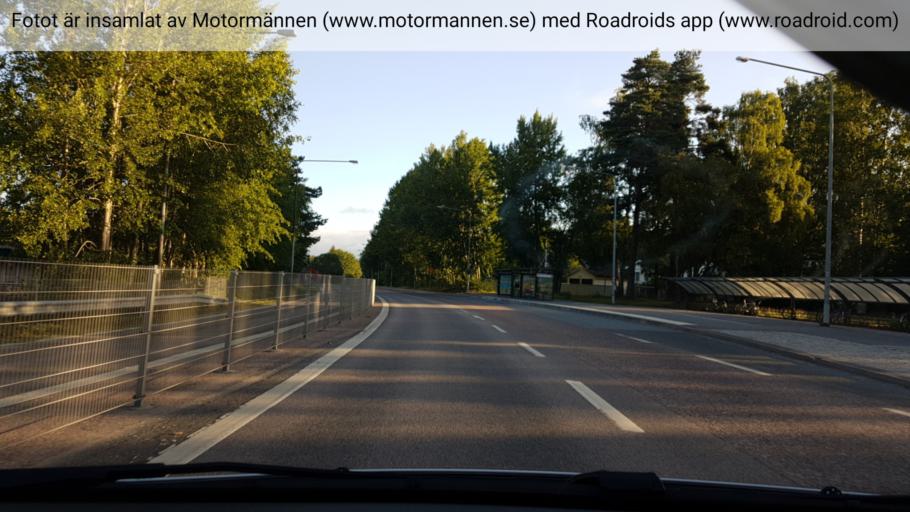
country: SE
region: Stockholm
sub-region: Tyreso Kommun
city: Bollmora
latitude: 59.2239
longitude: 18.2024
